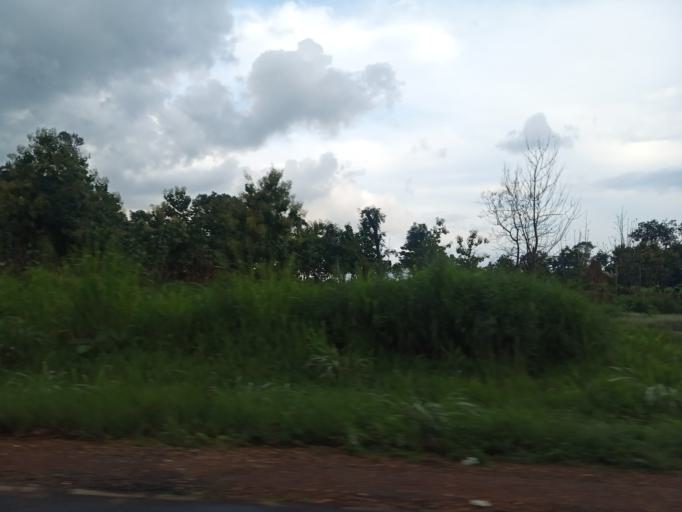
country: TG
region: Centrale
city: Sotouboua
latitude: 8.5915
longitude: 0.9938
